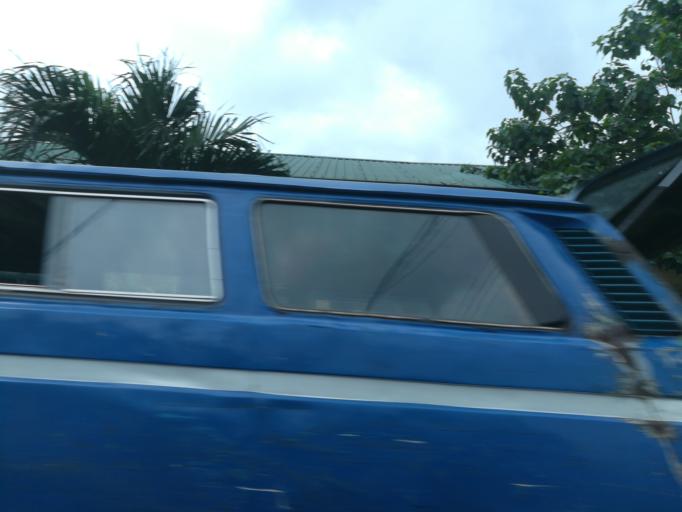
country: NG
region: Rivers
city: Port Harcourt
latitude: 4.7572
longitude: 7.0360
